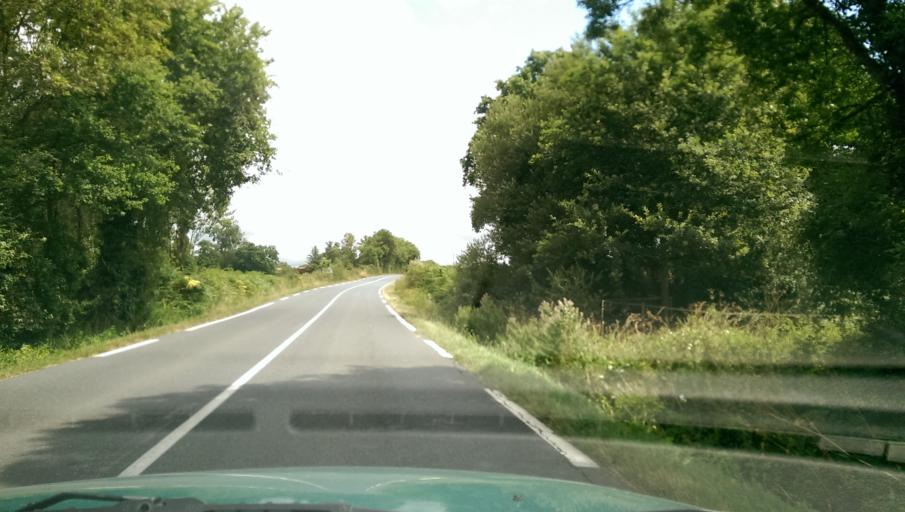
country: FR
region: Pays de la Loire
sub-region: Departement de la Loire-Atlantique
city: Remouille
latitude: 47.0744
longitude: -1.3722
